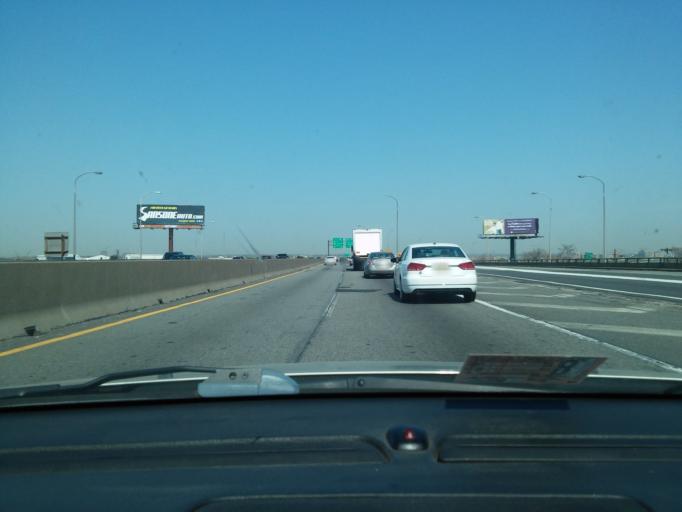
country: US
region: New Jersey
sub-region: Essex County
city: Newark
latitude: 40.7053
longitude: -74.1481
